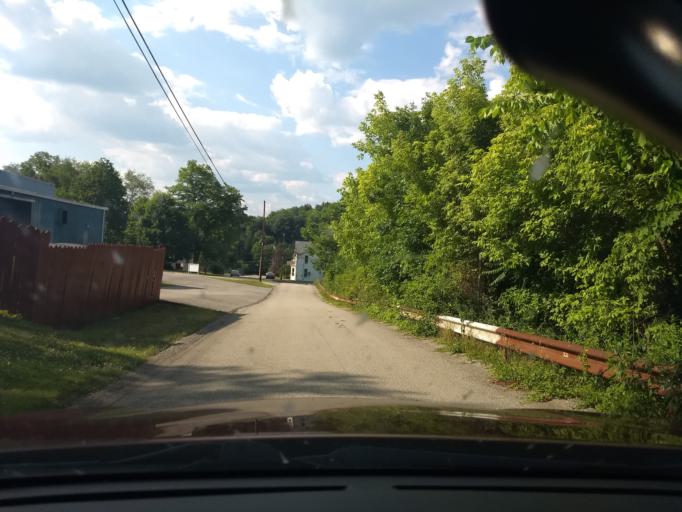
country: US
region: Pennsylvania
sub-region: Westmoreland County
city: Irwin
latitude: 40.3327
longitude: -79.7133
